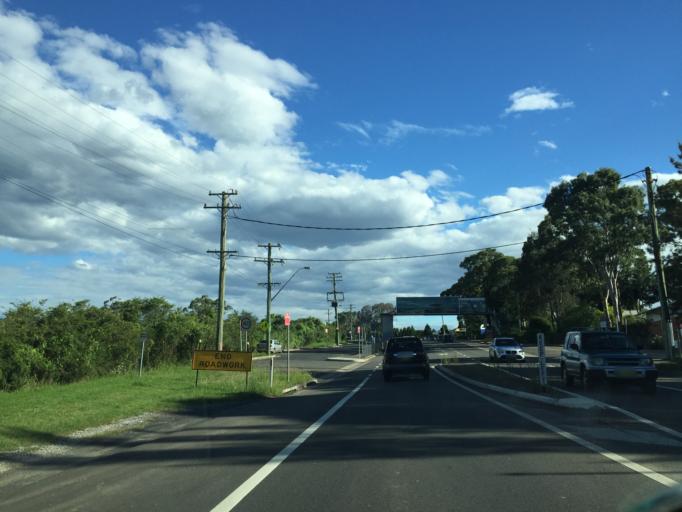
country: AU
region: New South Wales
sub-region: The Hills Shire
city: Glenhaven
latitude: -33.6854
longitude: 151.0275
